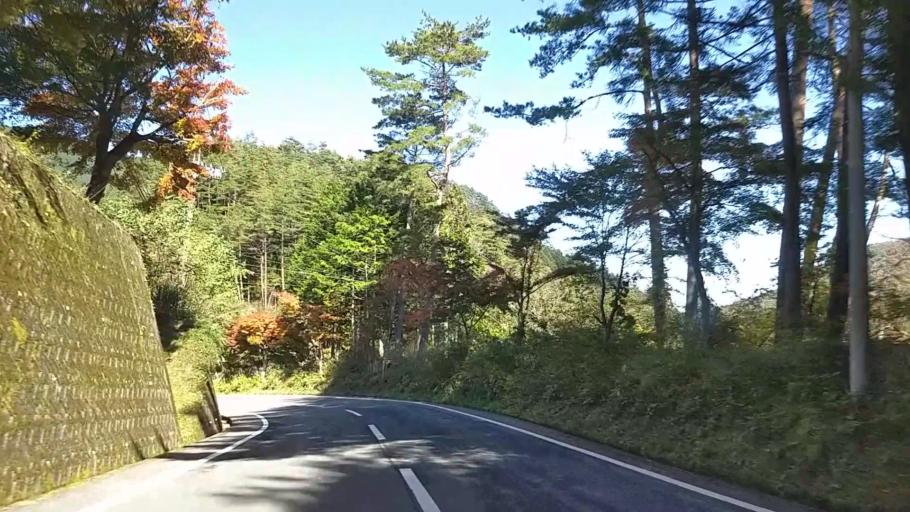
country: JP
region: Yamanashi
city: Otsuki
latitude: 35.7505
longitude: 138.9549
